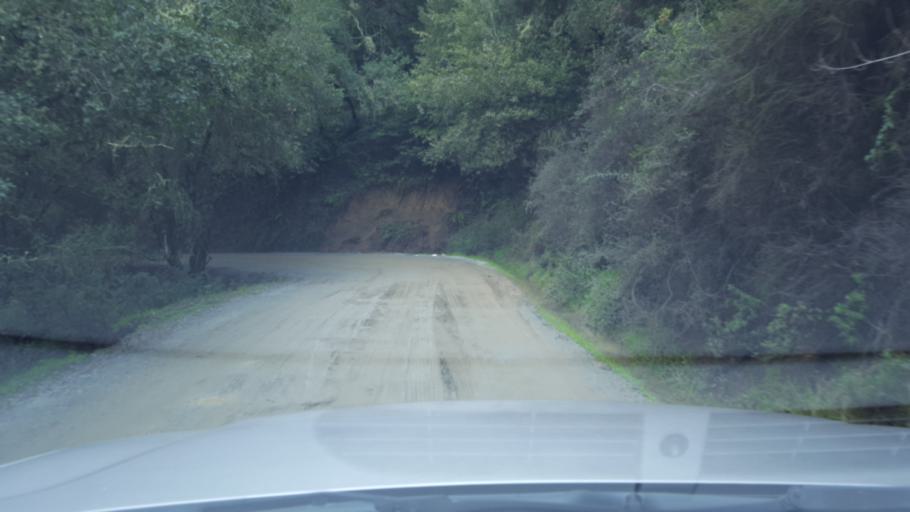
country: US
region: California
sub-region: Santa Cruz County
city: Interlaken
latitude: 37.0266
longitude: -121.7170
